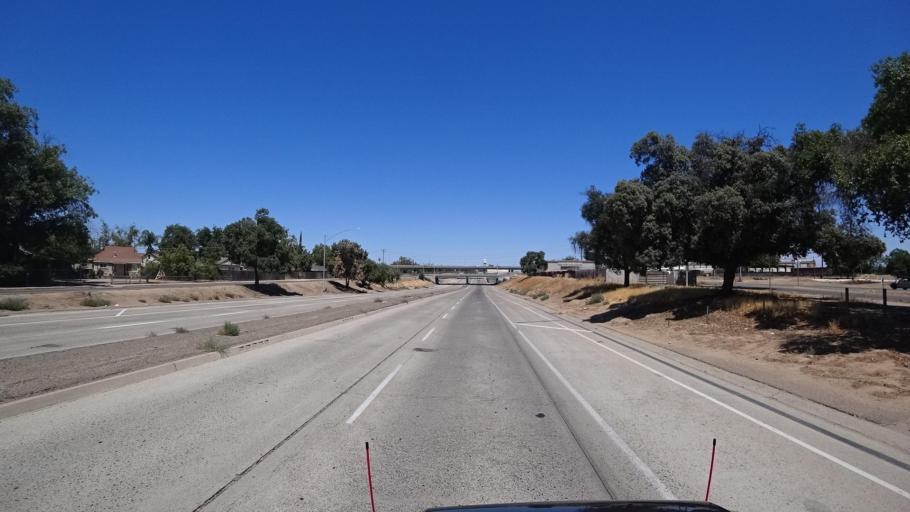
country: US
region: California
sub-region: Fresno County
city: Fresno
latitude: 36.7201
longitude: -119.7825
